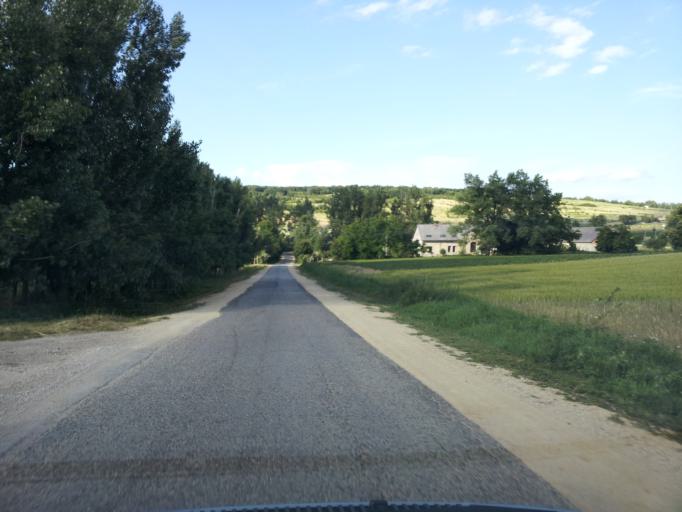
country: HU
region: Veszprem
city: Zirc
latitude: 47.2043
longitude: 17.8467
